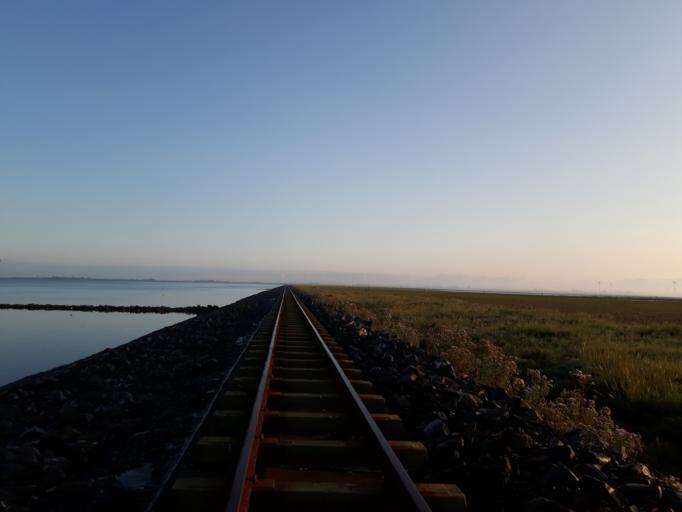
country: DE
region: Schleswig-Holstein
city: Dagebull
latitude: 54.6983
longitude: 8.7107
